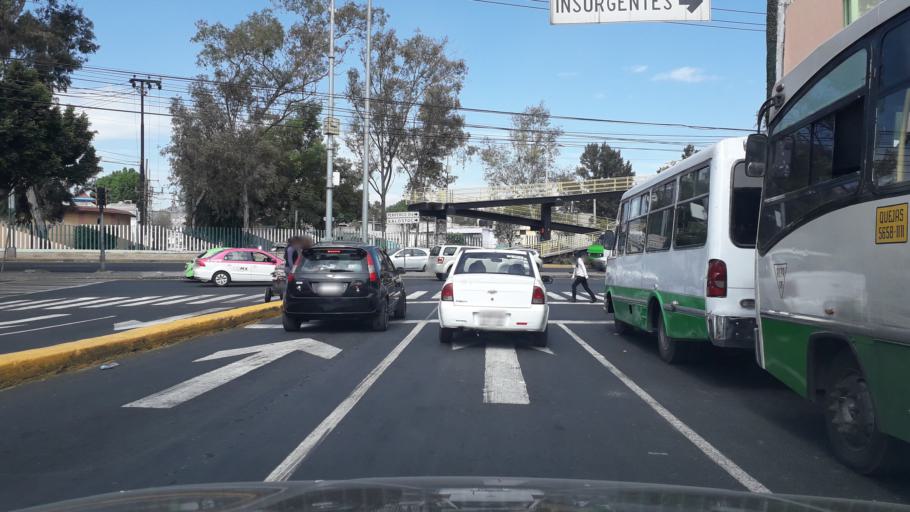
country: MX
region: Mexico City
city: Gustavo A. Madero
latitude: 19.5056
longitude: -99.0924
